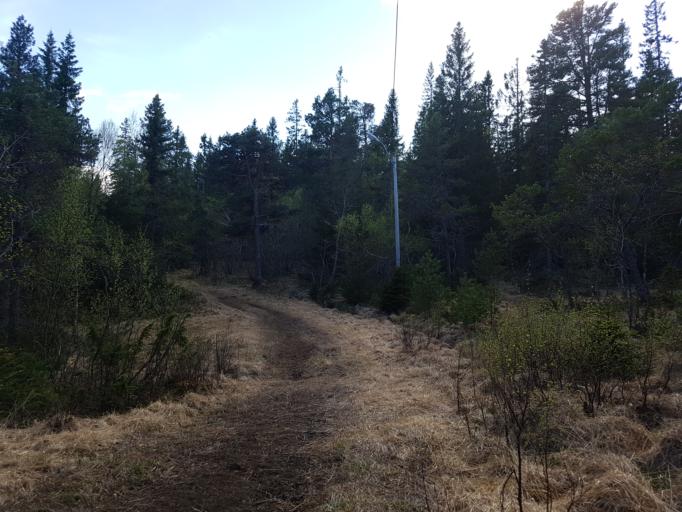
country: NO
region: Sor-Trondelag
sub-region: Trondheim
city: Trondheim
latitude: 63.4455
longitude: 10.2931
